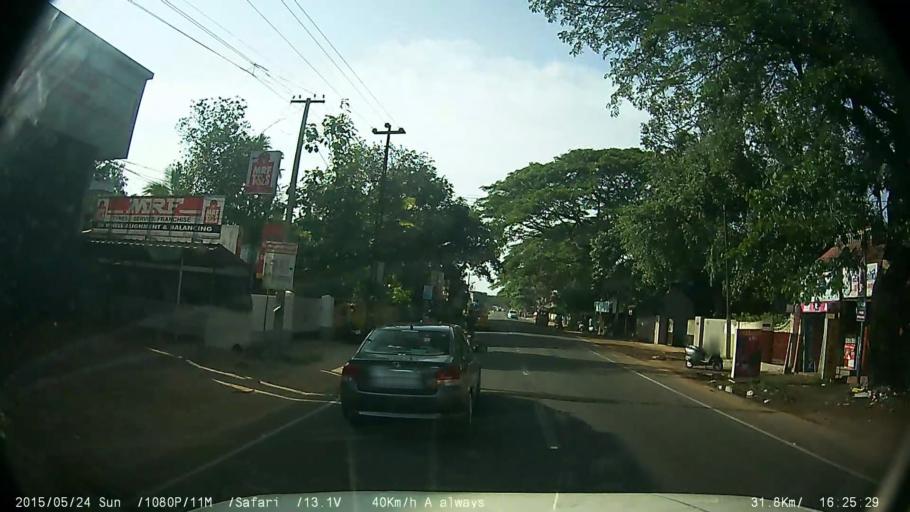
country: IN
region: Kerala
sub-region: Alappuzha
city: Alleppey
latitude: 9.5130
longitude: 76.3278
